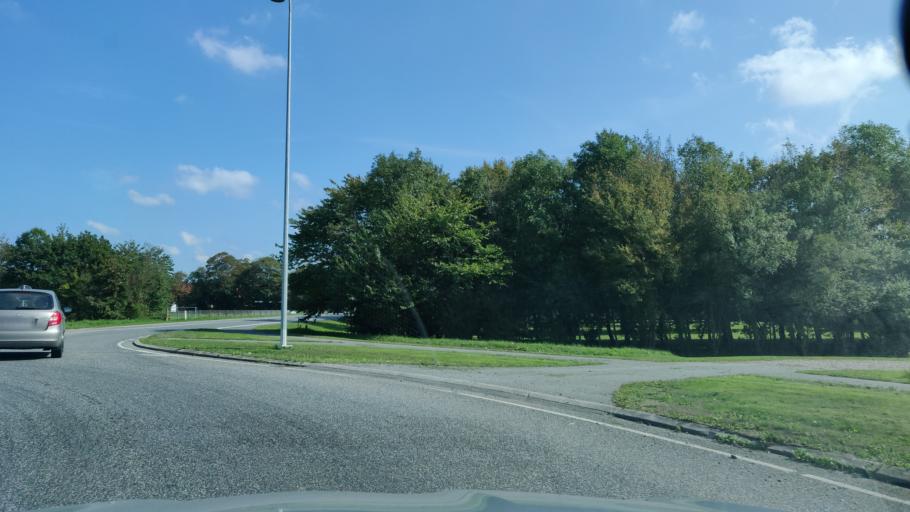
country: DK
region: Central Jutland
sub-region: Viborg Kommune
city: Viborg
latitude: 56.4488
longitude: 9.3423
